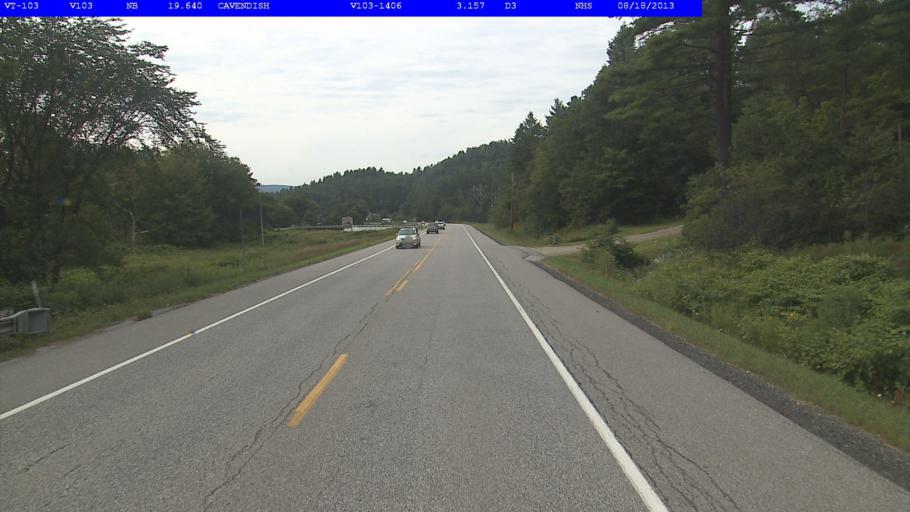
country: US
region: Vermont
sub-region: Windsor County
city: Chester
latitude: 43.3863
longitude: -72.6511
